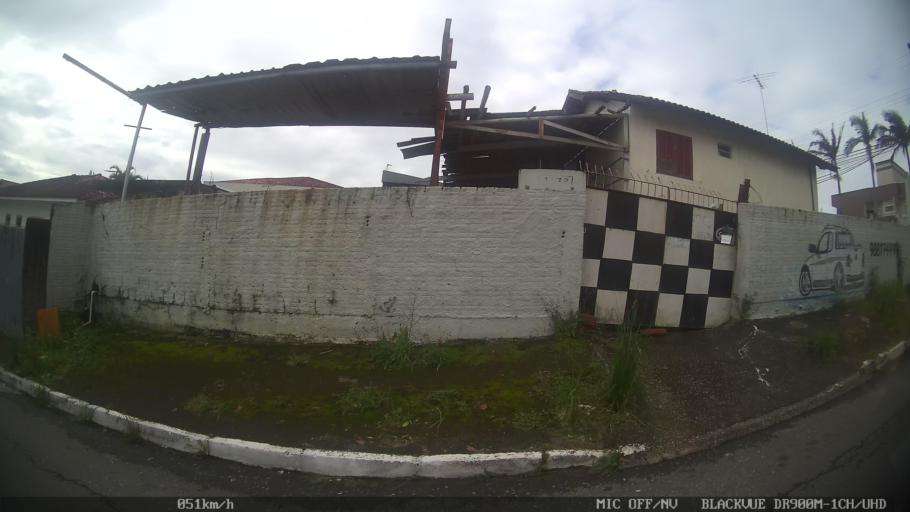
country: BR
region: Santa Catarina
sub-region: Sao Jose
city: Campinas
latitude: -27.5645
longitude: -48.6316
